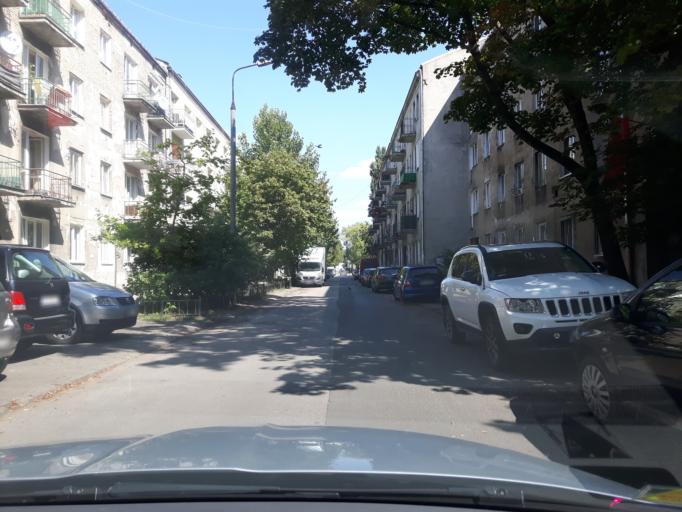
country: PL
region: Masovian Voivodeship
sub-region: Warszawa
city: Praga Polnoc
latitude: 52.2581
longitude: 21.0554
